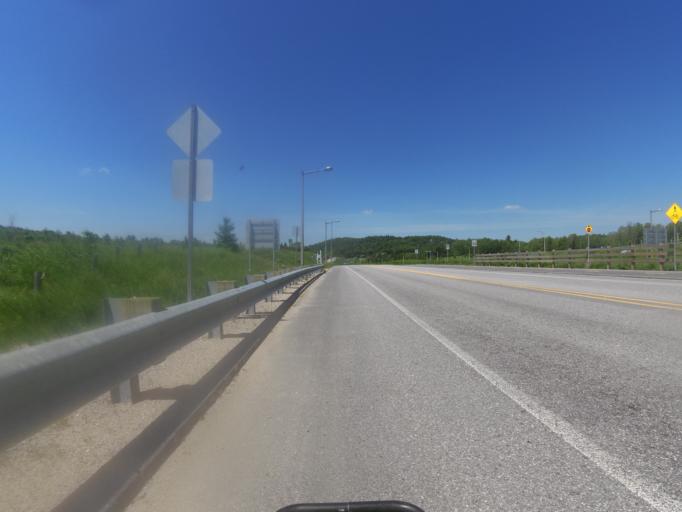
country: CA
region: Quebec
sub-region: Outaouais
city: Wakefield
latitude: 45.6273
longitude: -75.9386
